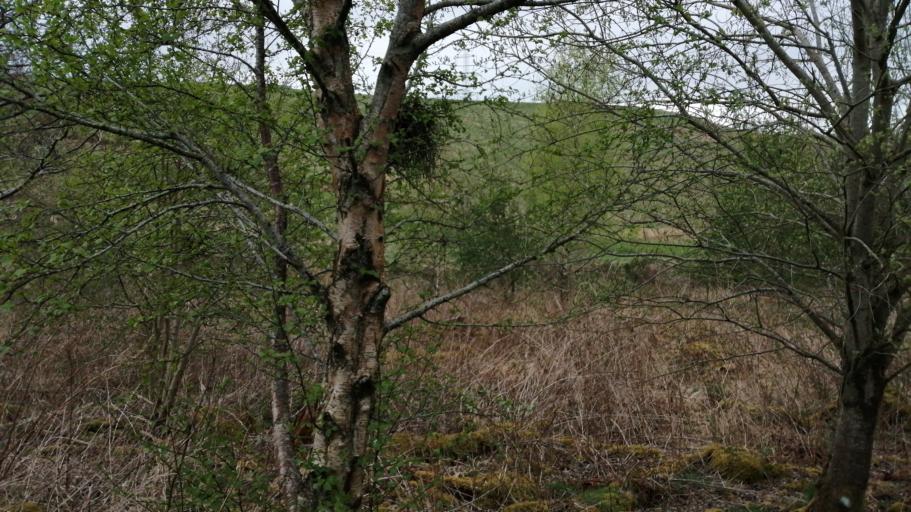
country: GB
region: Scotland
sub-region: Moray
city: Keith
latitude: 57.5353
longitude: -2.9336
